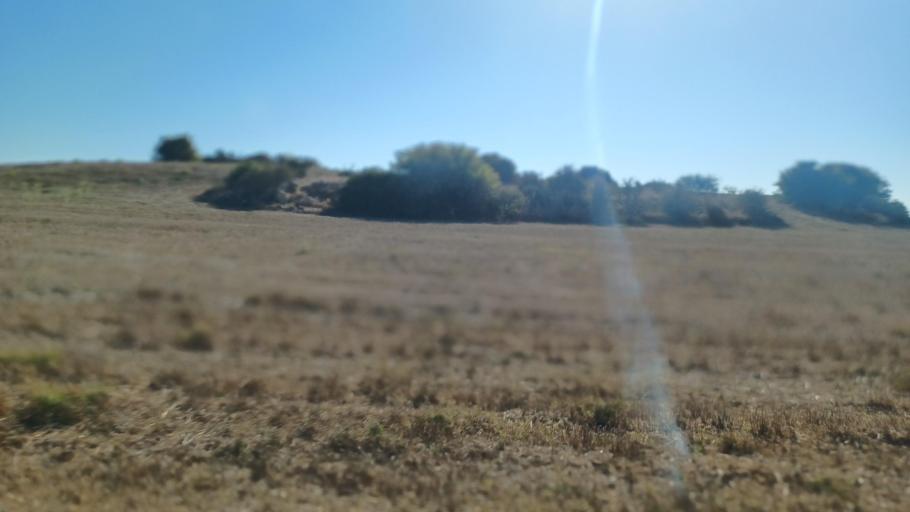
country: CY
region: Pafos
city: Mesogi
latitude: 34.8022
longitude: 32.4942
